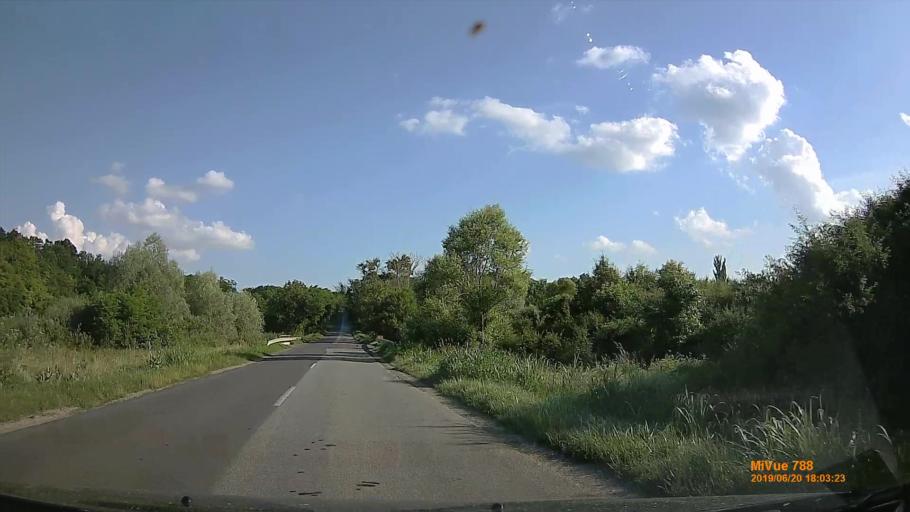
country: HU
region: Baranya
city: Szentlorinc
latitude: 46.0622
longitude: 17.9908
